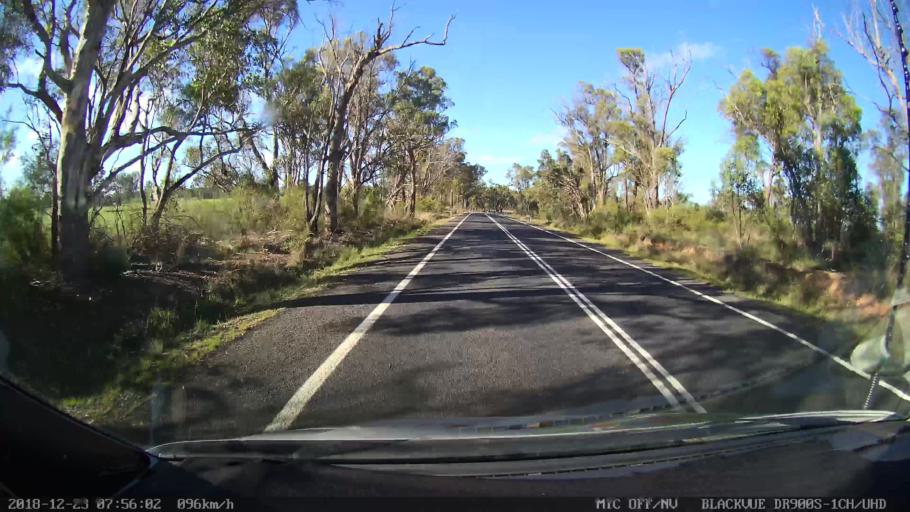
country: AU
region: New South Wales
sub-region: Armidale Dumaresq
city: Armidale
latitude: -30.5441
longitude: 151.7718
